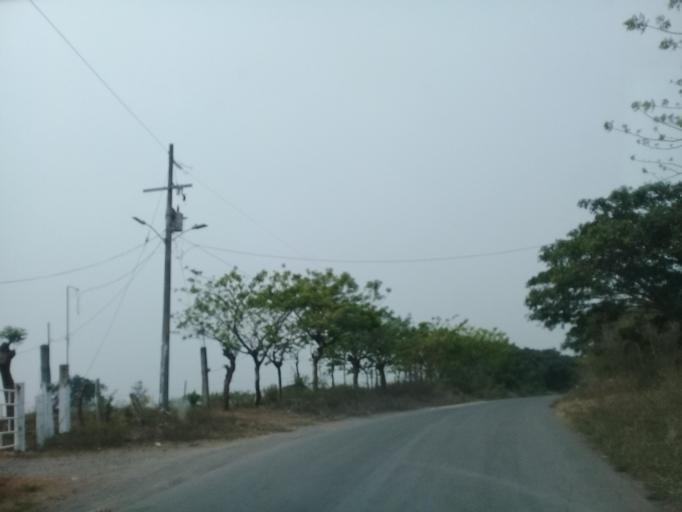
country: MX
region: Veracruz
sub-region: Medellin
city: La Laguna y Monte del Castillo
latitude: 18.9542
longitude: -96.1252
